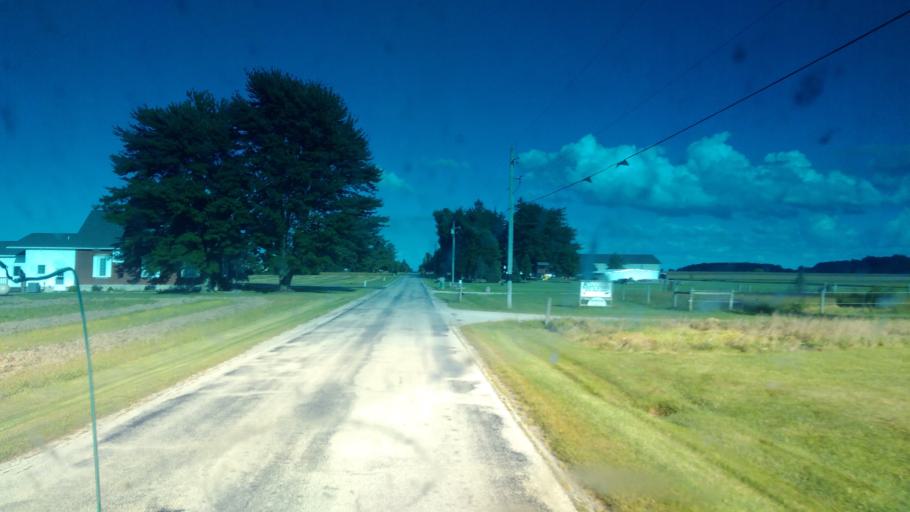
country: US
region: Ohio
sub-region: Hancock County
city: Arlington
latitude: 40.9357
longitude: -83.6356
